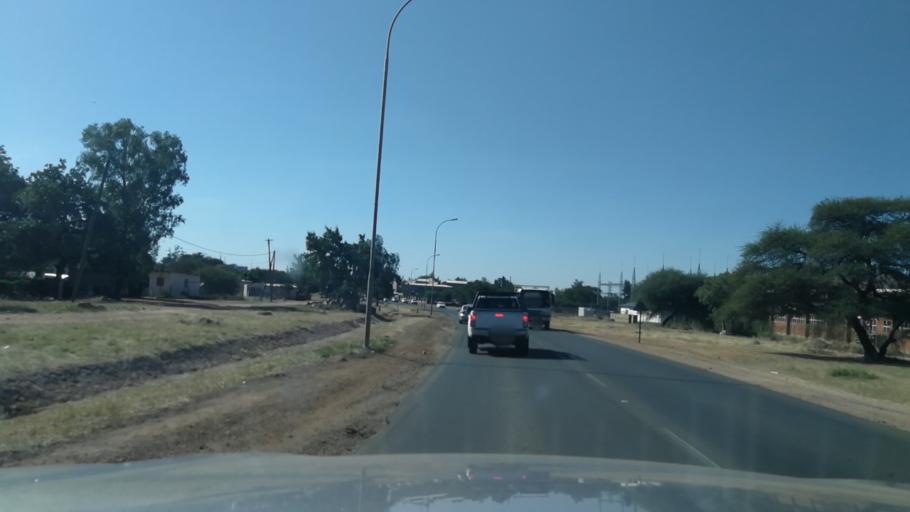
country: BW
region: South East
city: Gaborone
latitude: -24.6872
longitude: 25.9042
